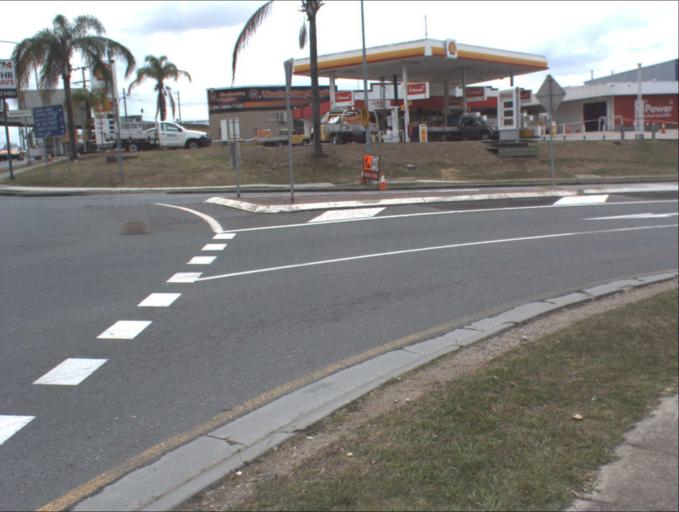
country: AU
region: Queensland
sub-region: Logan
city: Beenleigh
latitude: -27.7149
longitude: 153.1942
